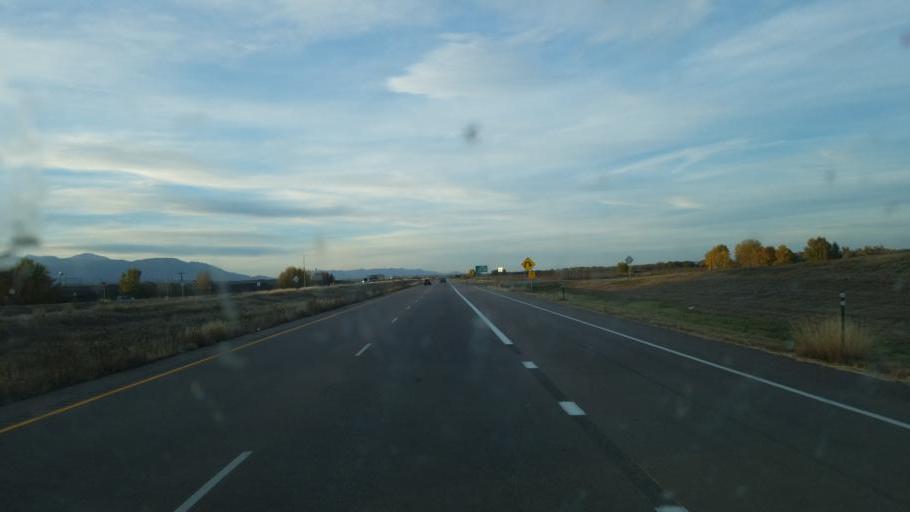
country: US
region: Colorado
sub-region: El Paso County
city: Fountain
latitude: 38.5875
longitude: -104.6694
